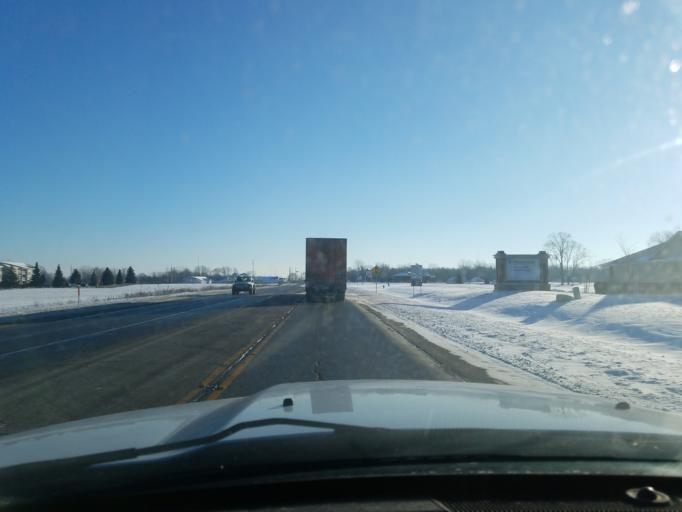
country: US
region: Indiana
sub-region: Noble County
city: Kendallville
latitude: 41.4524
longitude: -85.2976
